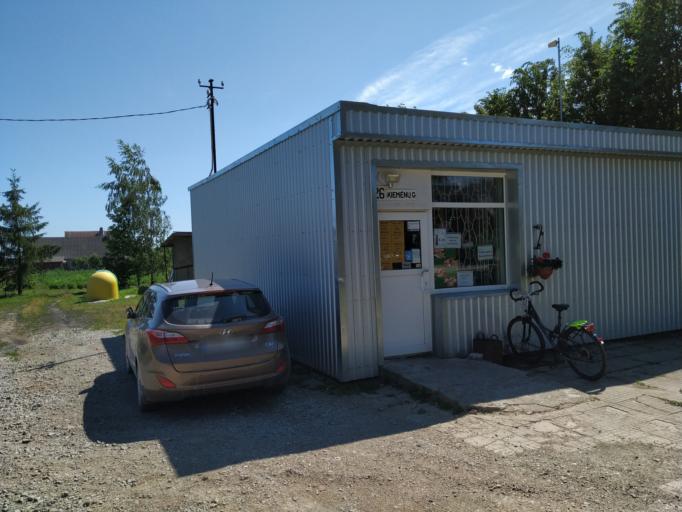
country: LV
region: Bauskas Rajons
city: Bauska
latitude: 56.2520
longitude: 24.3023
